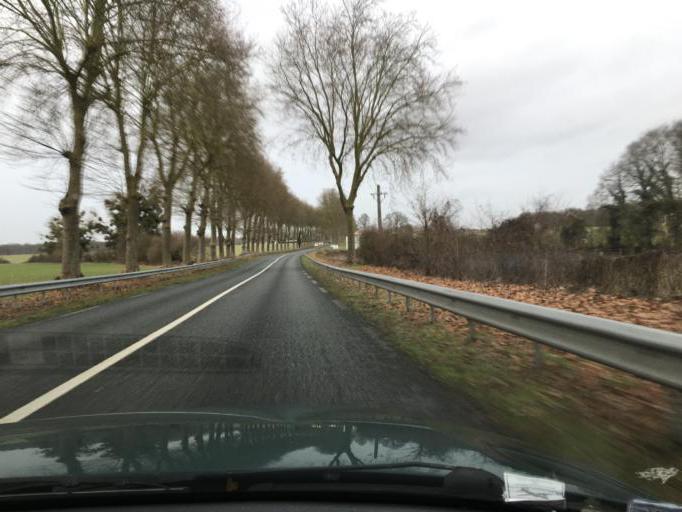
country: FR
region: Picardie
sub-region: Departement de l'Oise
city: La Chapelle-en-Serval
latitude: 49.1446
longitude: 2.5416
